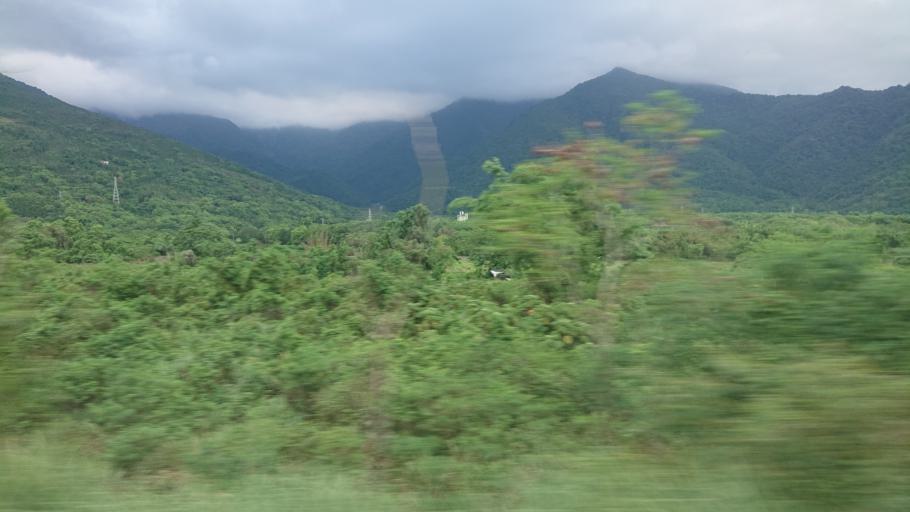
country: TW
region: Taiwan
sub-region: Hualien
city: Hualian
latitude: 23.6266
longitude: 121.4010
